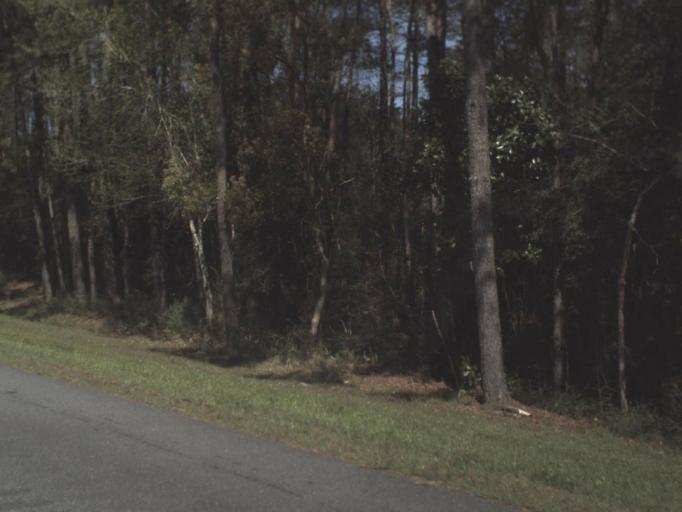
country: US
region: Florida
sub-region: Walton County
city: DeFuniak Springs
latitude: 30.6912
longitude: -86.0712
